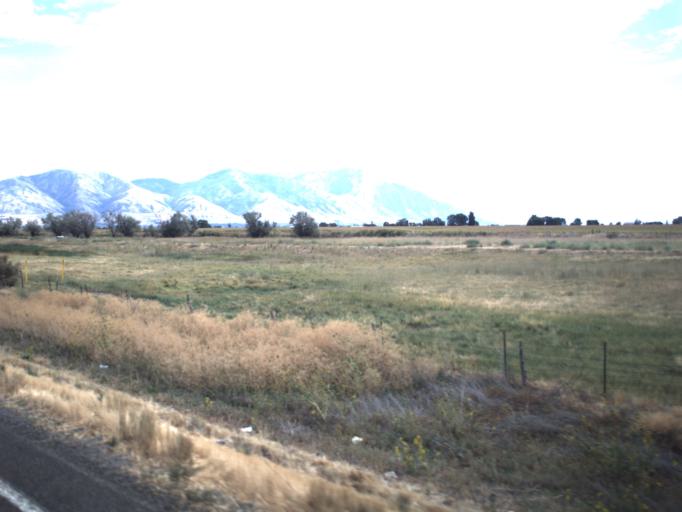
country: US
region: Utah
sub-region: Box Elder County
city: Honeyville
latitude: 41.5601
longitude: -112.1530
